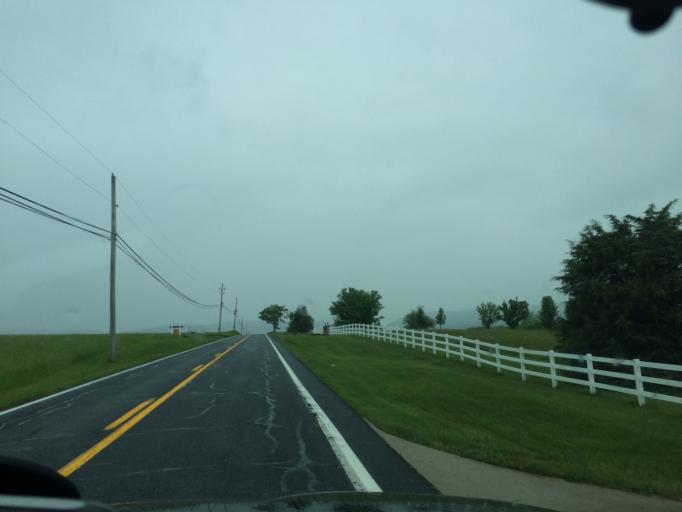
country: US
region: Maryland
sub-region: Frederick County
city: Thurmont
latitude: 39.6147
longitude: -77.3647
